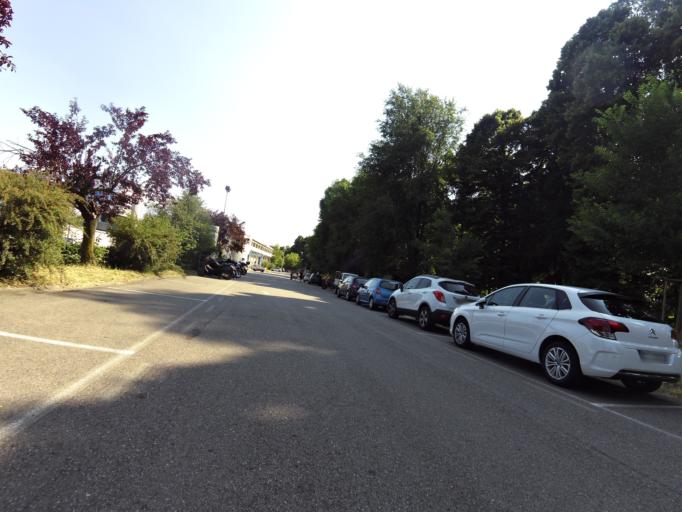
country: IT
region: Lombardy
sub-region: Citta metropolitana di Milano
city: Novegro-Tregarezzo-San Felice
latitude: 45.4742
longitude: 9.2887
